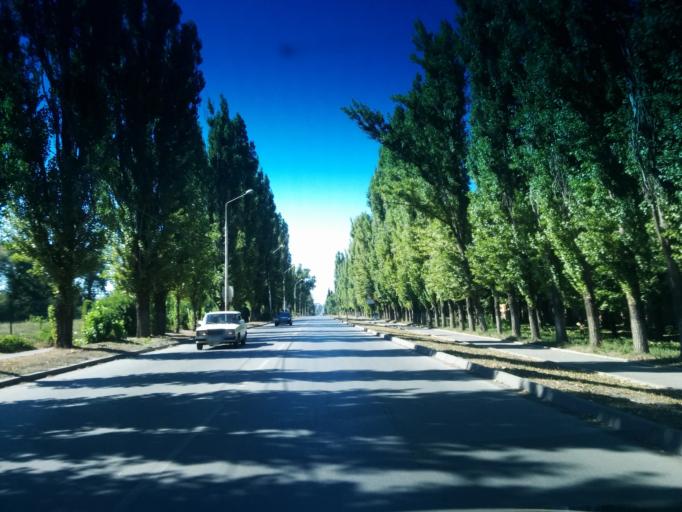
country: RU
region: Rostov
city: Shakhty
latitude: 47.6915
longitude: 40.2519
